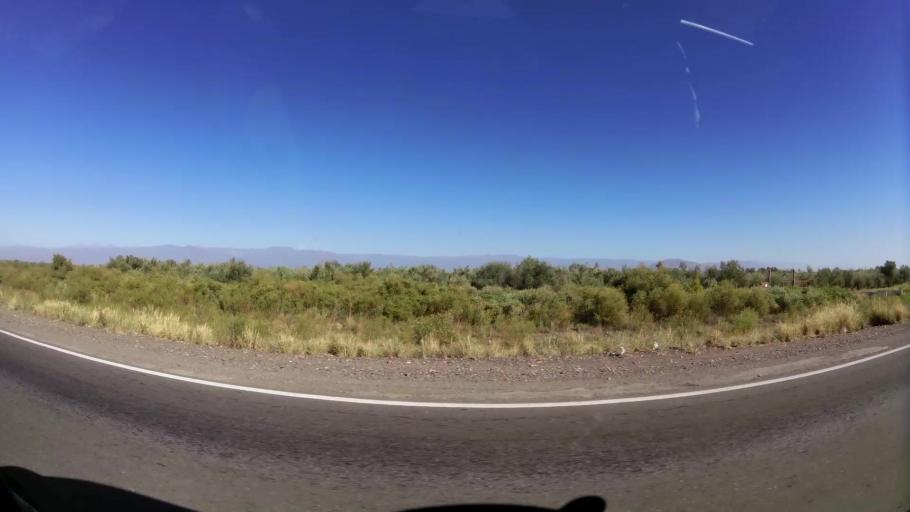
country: AR
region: Mendoza
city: General Lavalle
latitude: -32.7081
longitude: -68.6760
